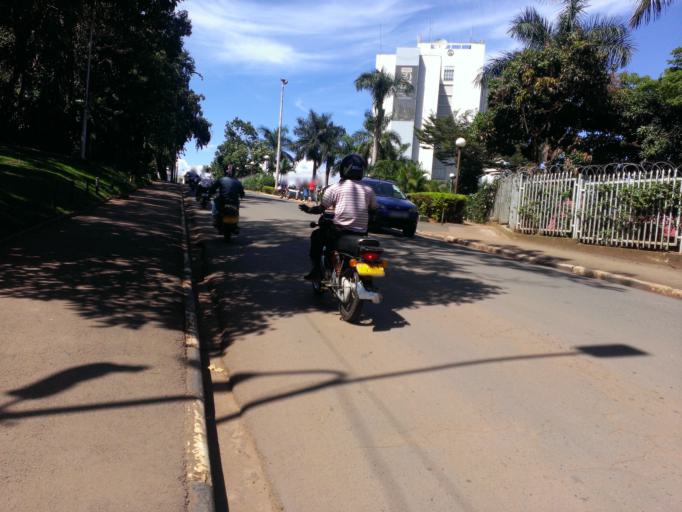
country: UG
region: Central Region
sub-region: Kampala District
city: Kampala
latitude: 0.3167
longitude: 32.5815
